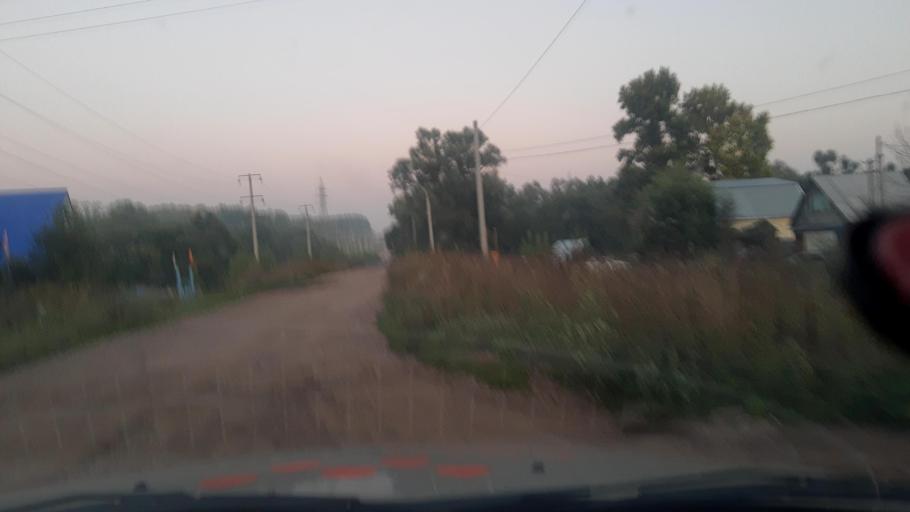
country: RU
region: Bashkortostan
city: Blagoveshchensk
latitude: 55.0500
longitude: 55.9825
